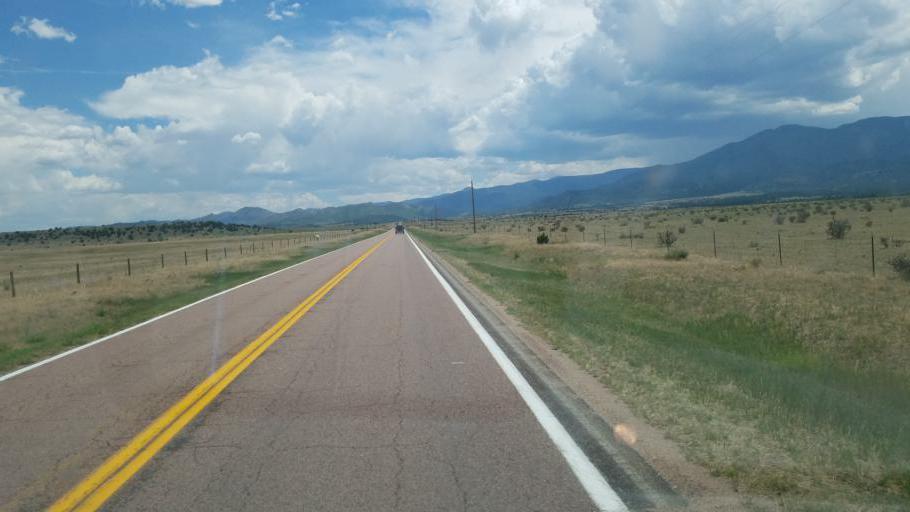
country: US
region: Colorado
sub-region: Fremont County
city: Florence
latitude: 38.2905
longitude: -105.0875
